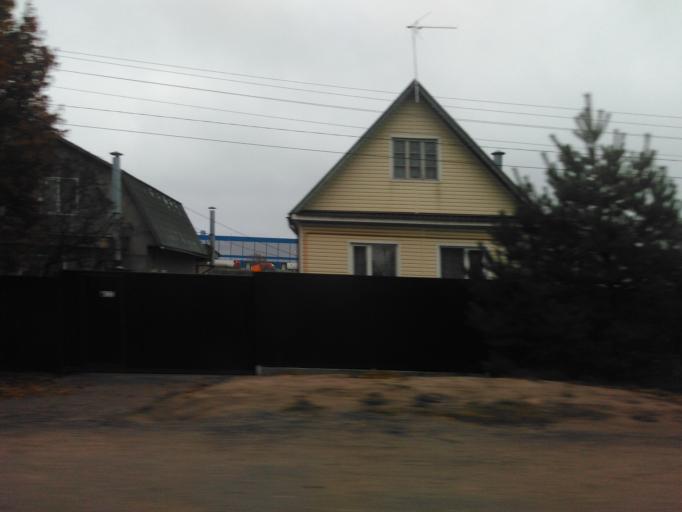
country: RU
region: Moskovskaya
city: Sofrino
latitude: 56.1199
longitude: 37.9654
